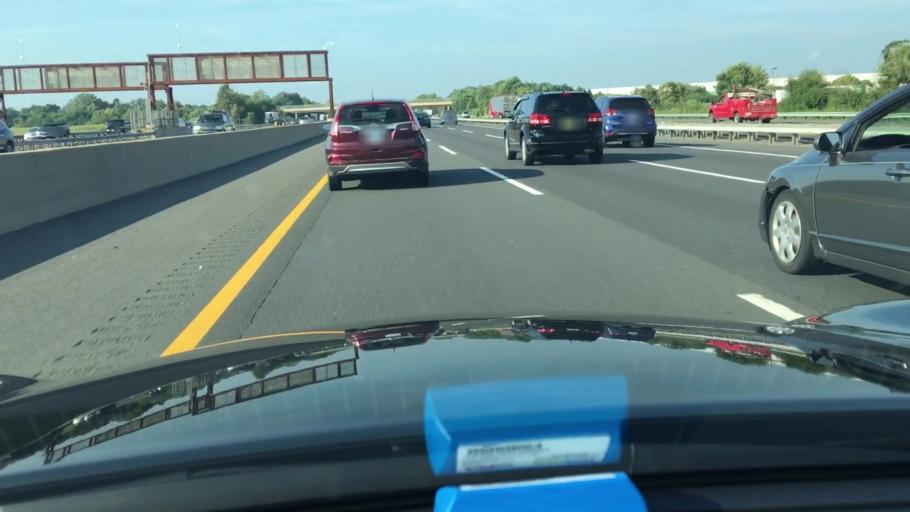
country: US
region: New Jersey
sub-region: Middlesex County
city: Helmetta
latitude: 40.3908
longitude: -74.4556
